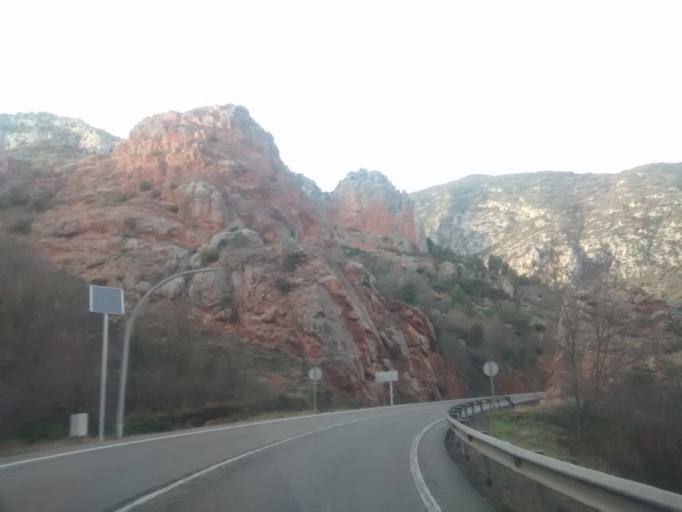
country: ES
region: Catalonia
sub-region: Provincia de Lleida
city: Coll de Nargo
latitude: 42.1758
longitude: 1.3178
